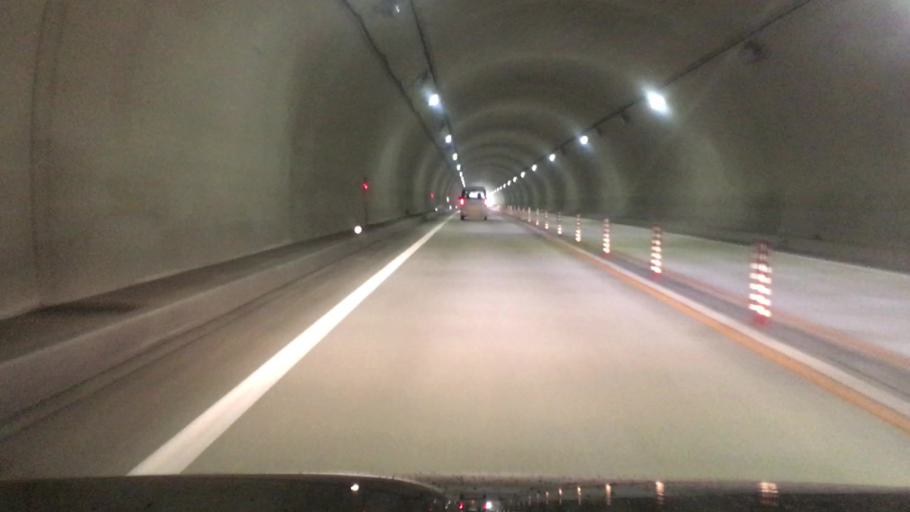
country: JP
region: Hyogo
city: Toyooka
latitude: 35.4443
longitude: 134.7668
